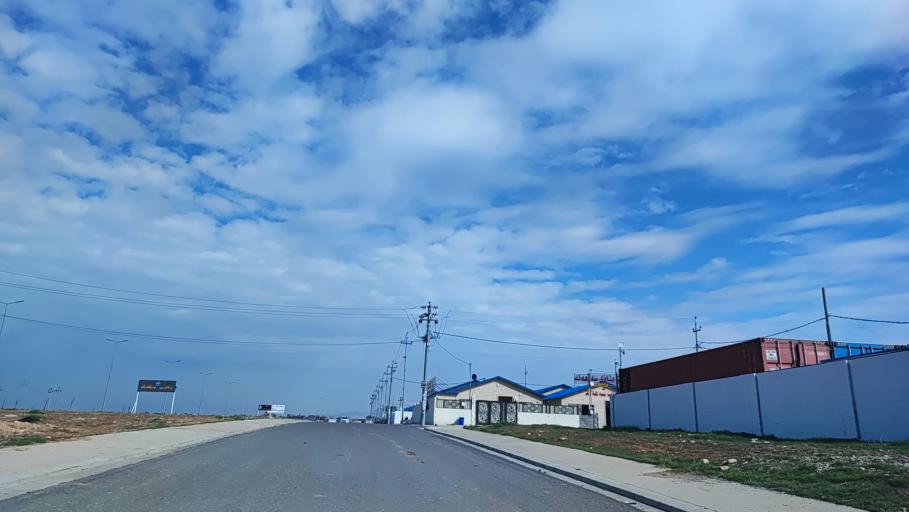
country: IQ
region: Arbil
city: Erbil
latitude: 36.2854
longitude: 44.0728
